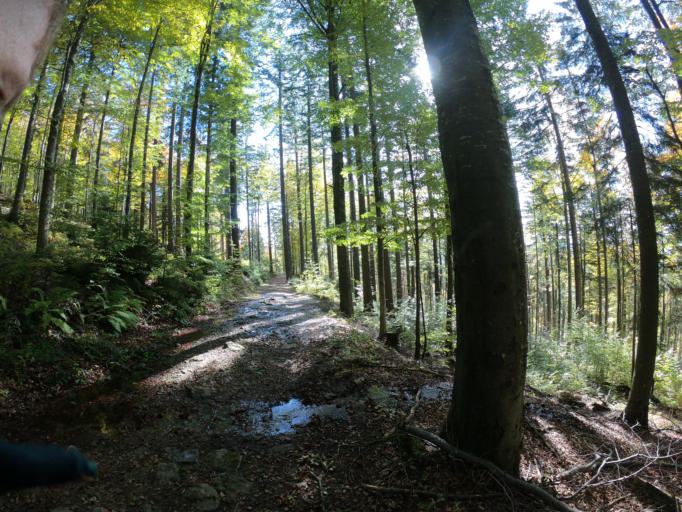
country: DE
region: Bavaria
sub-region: Lower Bavaria
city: Bodenmais
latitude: 49.0833
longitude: 13.1149
